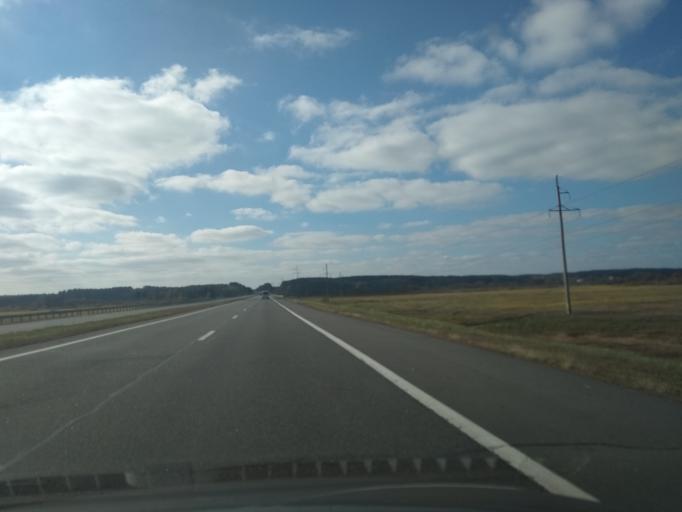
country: BY
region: Minsk
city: Novy Svyerzhan'
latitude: 53.5032
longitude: 26.6600
